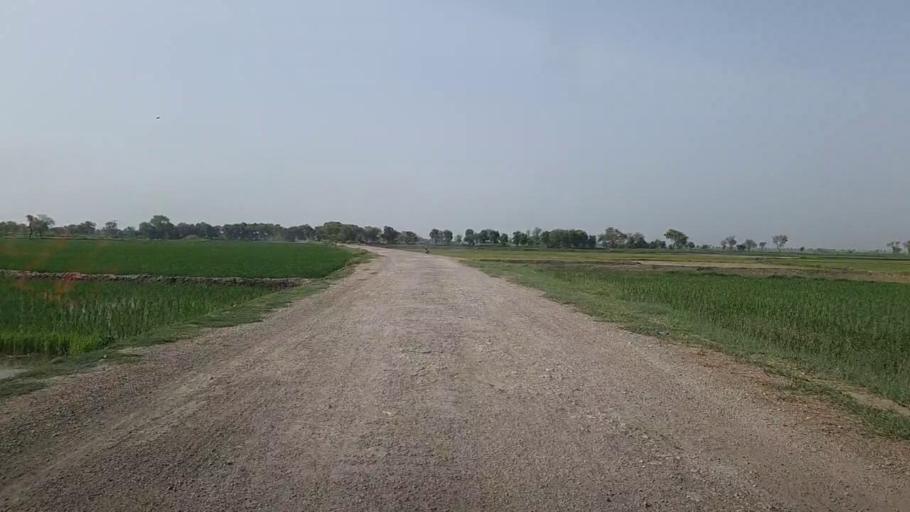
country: PK
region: Sindh
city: Mehar
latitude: 27.1075
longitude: 67.8205
